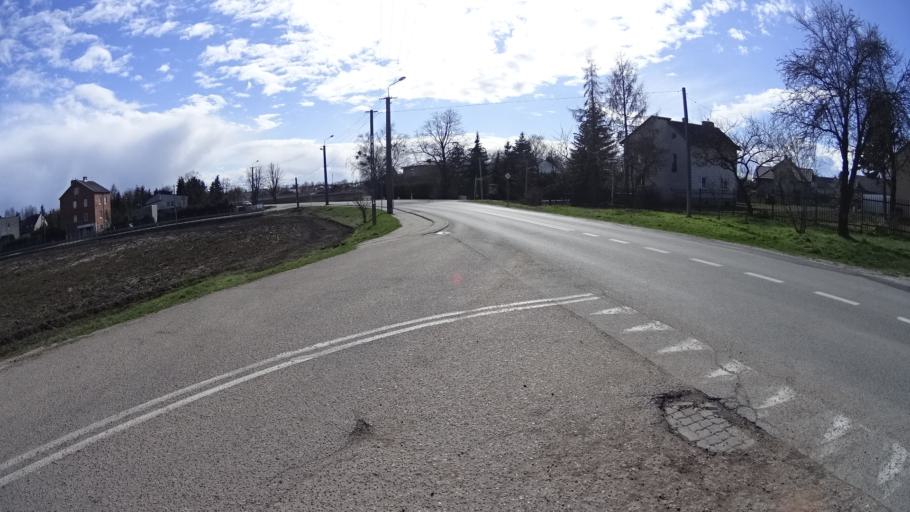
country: PL
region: Masovian Voivodeship
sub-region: Powiat warszawski zachodni
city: Jozefow
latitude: 52.2049
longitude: 20.6962
